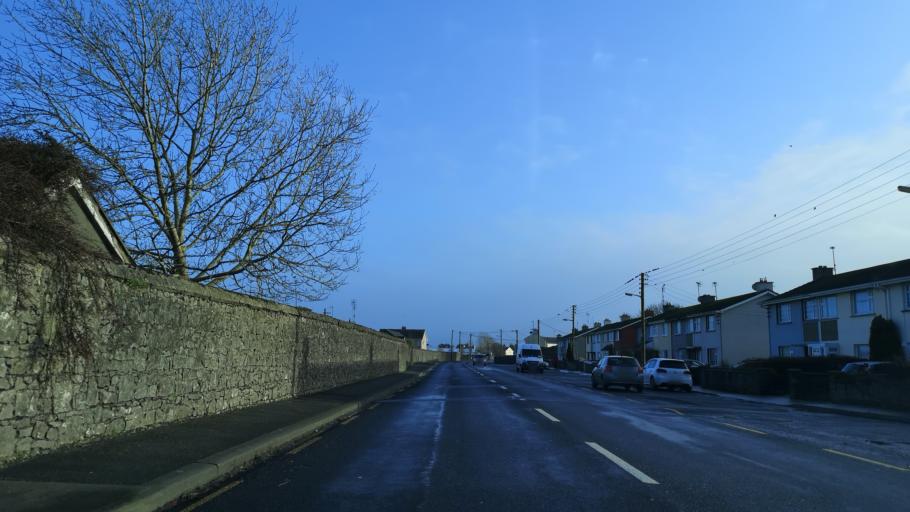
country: IE
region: Connaught
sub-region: County Galway
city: Tuam
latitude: 53.5096
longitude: -8.8423
